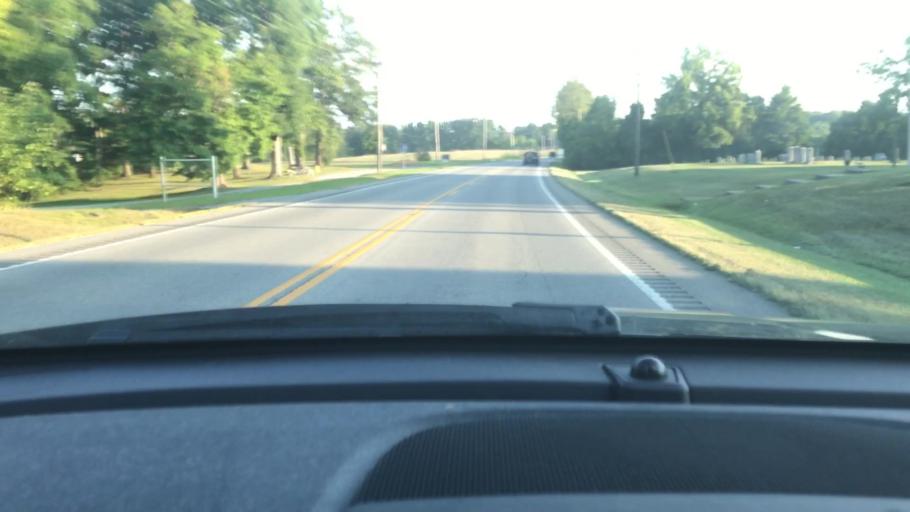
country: US
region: Tennessee
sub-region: Dickson County
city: Charlotte
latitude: 36.1484
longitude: -87.3561
